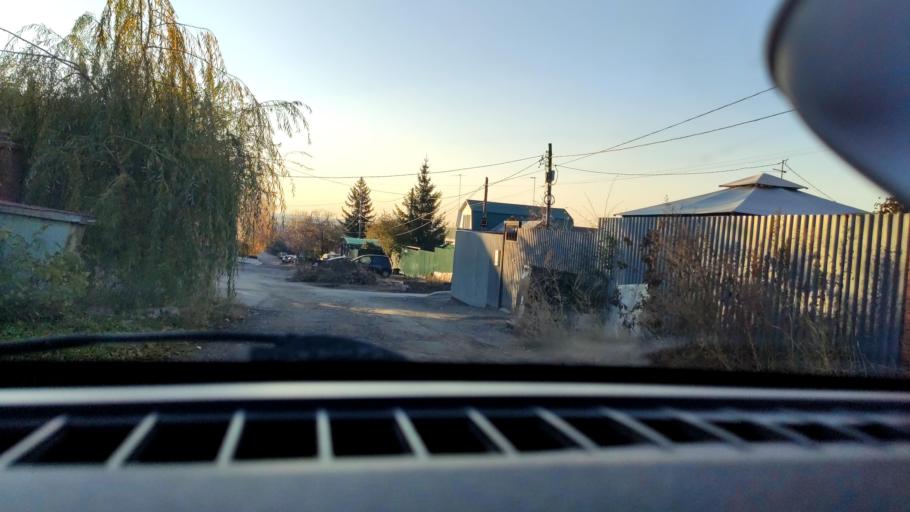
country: RU
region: Samara
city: Samara
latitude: 53.1787
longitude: 50.1818
